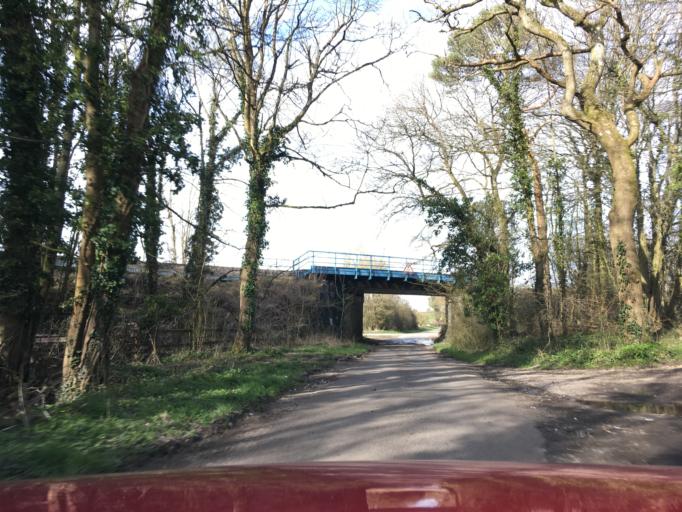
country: GB
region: England
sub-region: Wiltshire
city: Luckington
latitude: 51.5355
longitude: -2.2421
